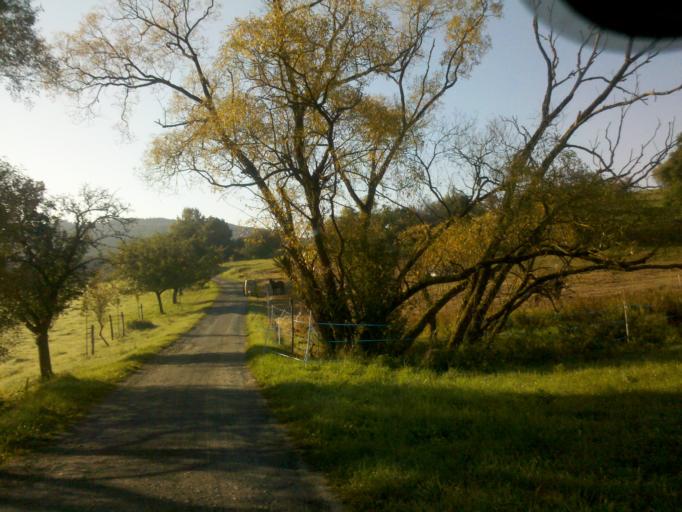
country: DE
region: Hesse
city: Herborn
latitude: 50.6937
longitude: 8.3348
